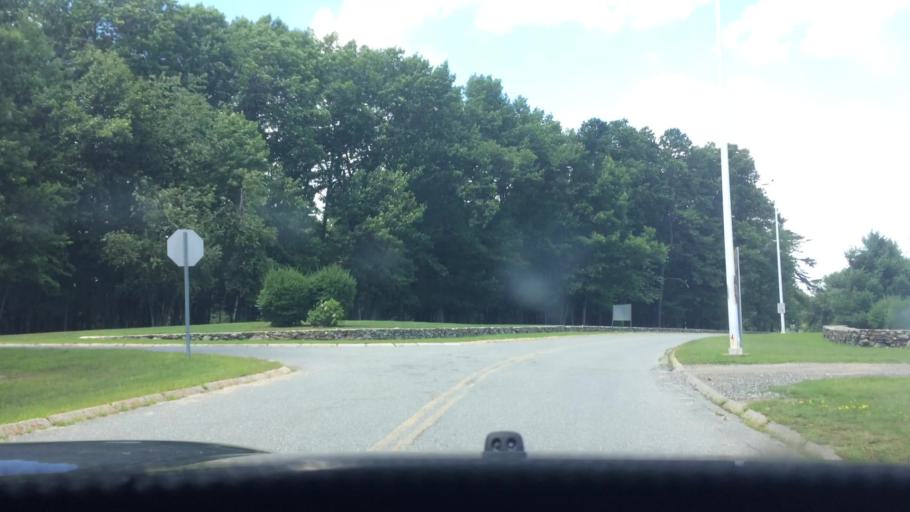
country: US
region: Massachusetts
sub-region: Middlesex County
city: Shirley
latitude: 42.5270
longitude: -71.6261
